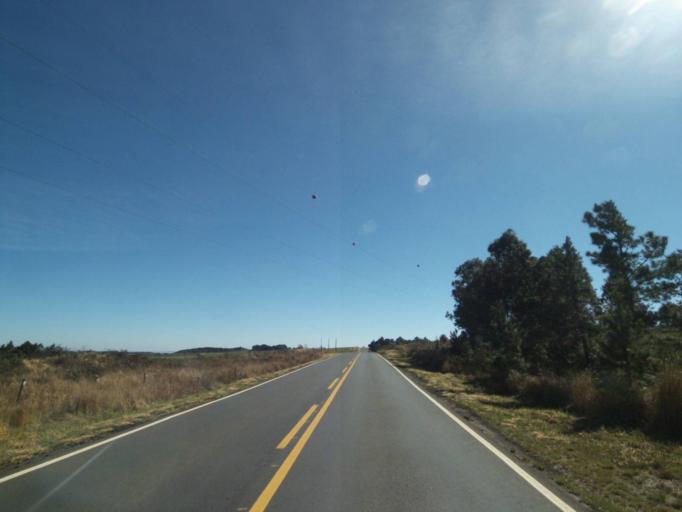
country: BR
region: Parana
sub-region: Castro
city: Castro
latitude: -24.6874
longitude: -50.2097
